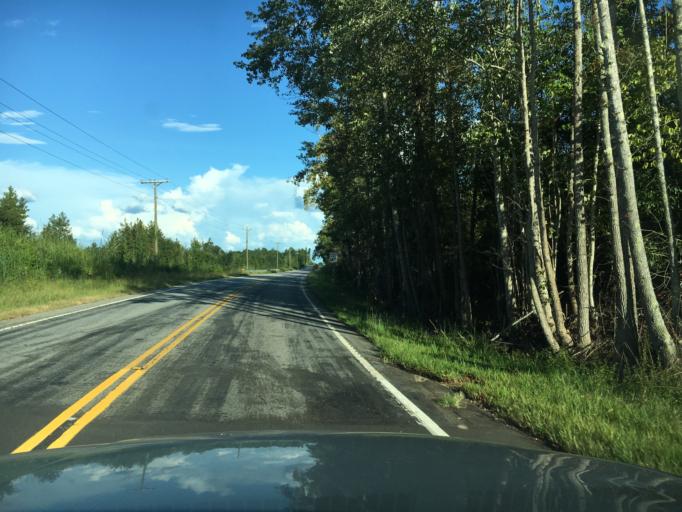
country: US
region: South Carolina
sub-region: Greenville County
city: Five Forks
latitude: 34.8001
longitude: -82.1539
